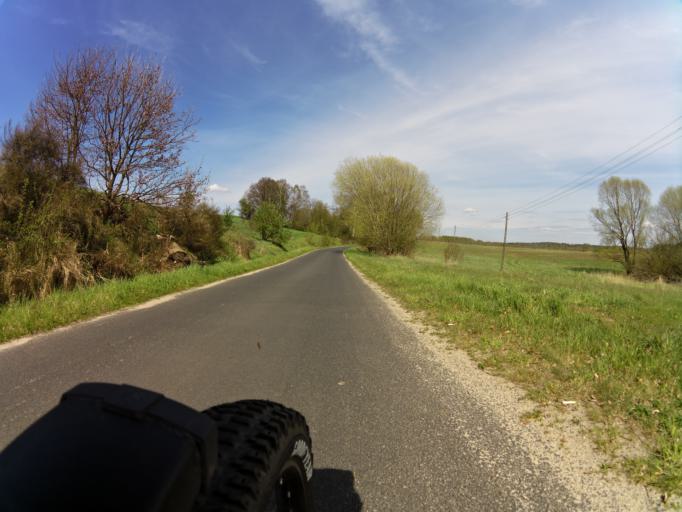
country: PL
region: West Pomeranian Voivodeship
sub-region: Powiat lobeski
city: Resko
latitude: 53.7859
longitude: 15.4240
